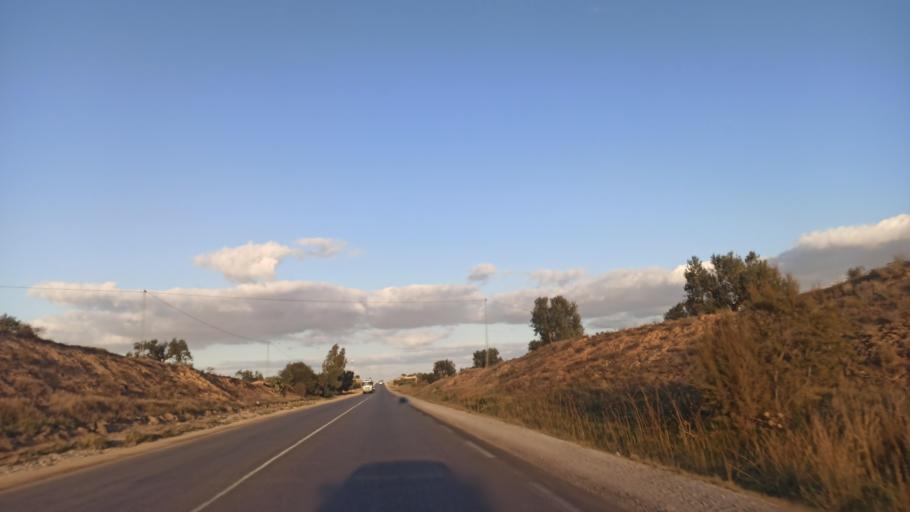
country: TN
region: Al Qayrawan
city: Sbikha
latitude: 35.8779
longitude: 10.2250
